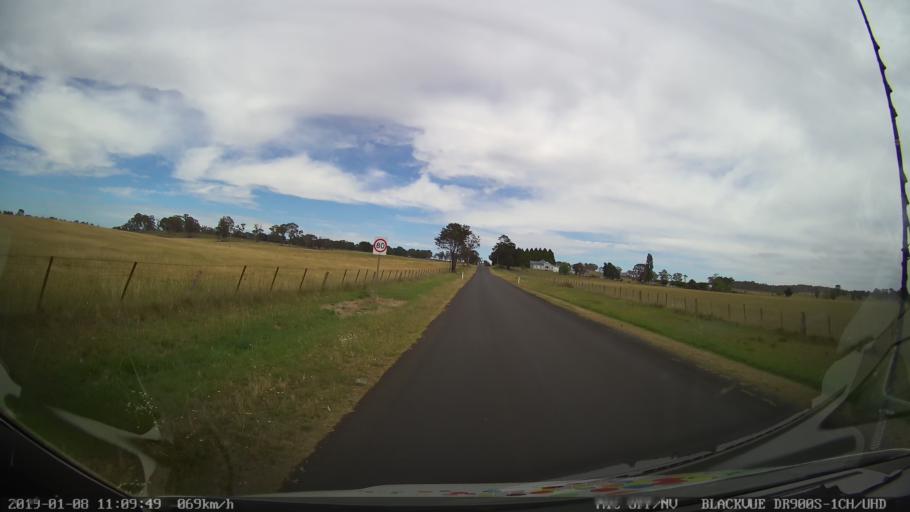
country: AU
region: New South Wales
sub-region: Guyra
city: Guyra
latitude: -30.2265
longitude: 151.6429
